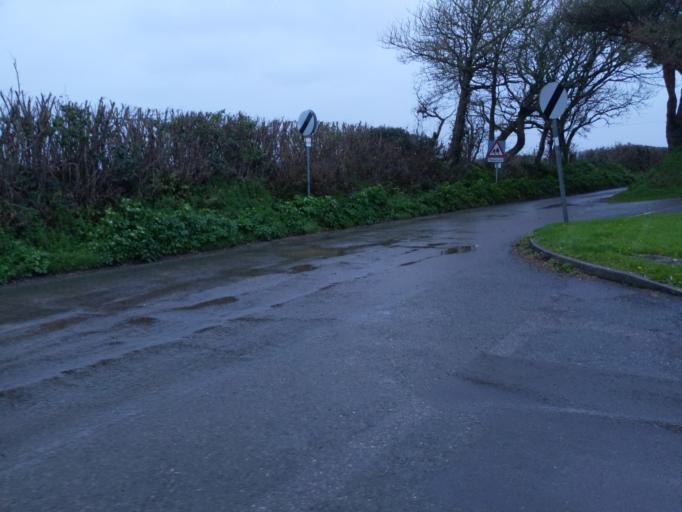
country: GB
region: England
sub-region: Devon
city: Yealmpton
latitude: 50.3234
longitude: -4.0311
